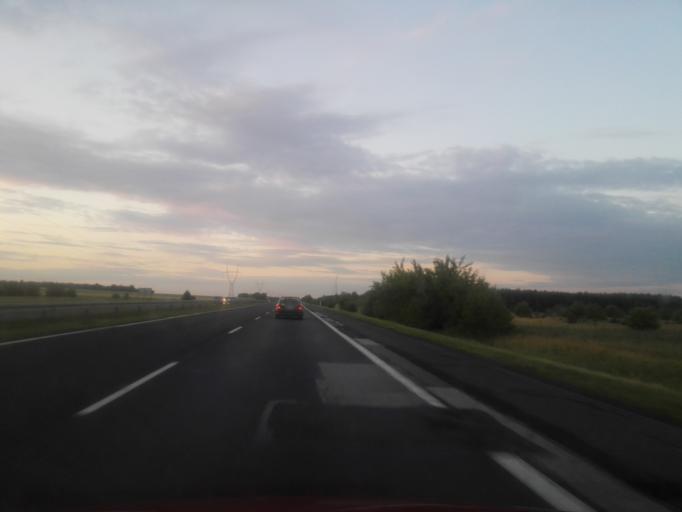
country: PL
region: Lodz Voivodeship
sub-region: Powiat radomszczanski
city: Radomsko
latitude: 51.1223
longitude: 19.4052
